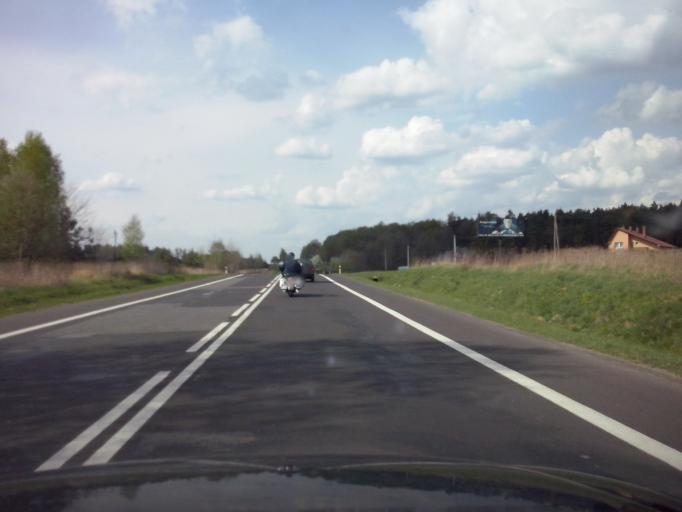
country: PL
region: Subcarpathian Voivodeship
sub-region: Powiat rzeszowski
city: Gorno
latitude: 50.2930
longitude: 22.1333
